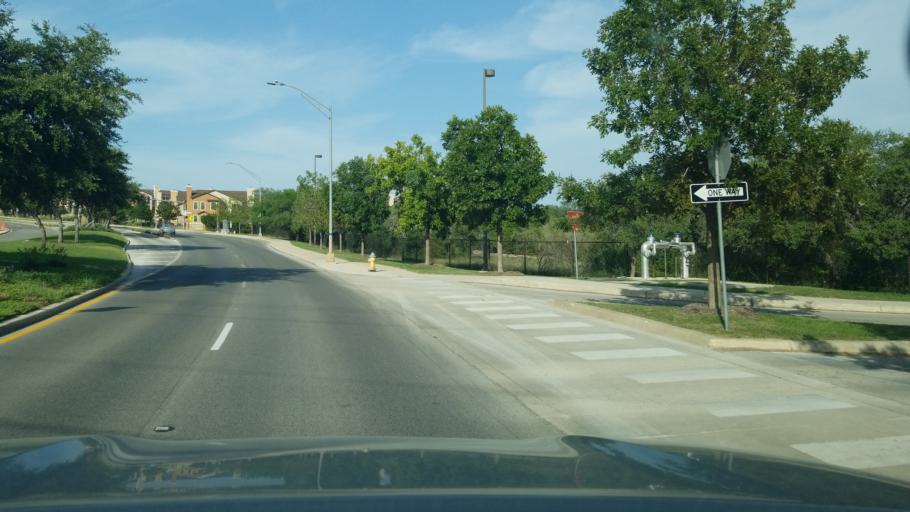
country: US
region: Texas
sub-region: Bexar County
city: Hollywood Park
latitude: 29.6458
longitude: -98.4677
